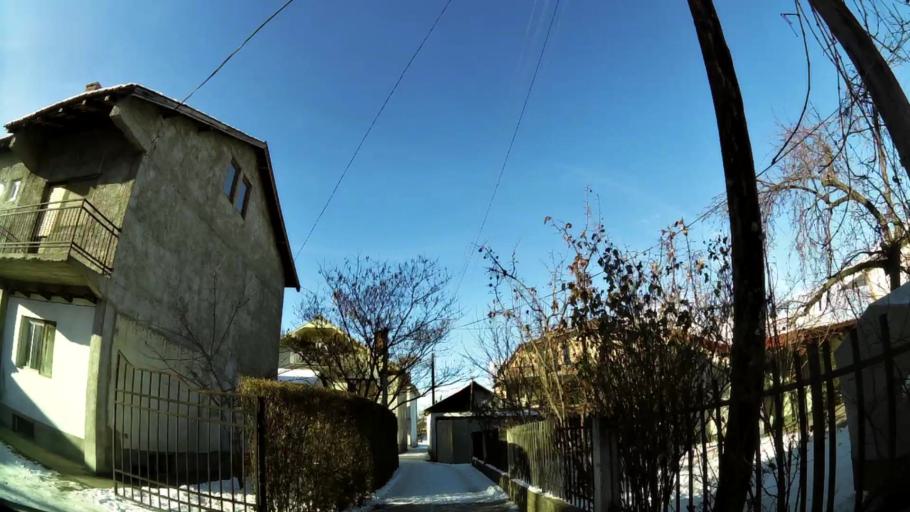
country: MK
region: Saraj
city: Saraj
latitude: 42.0098
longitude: 21.3444
